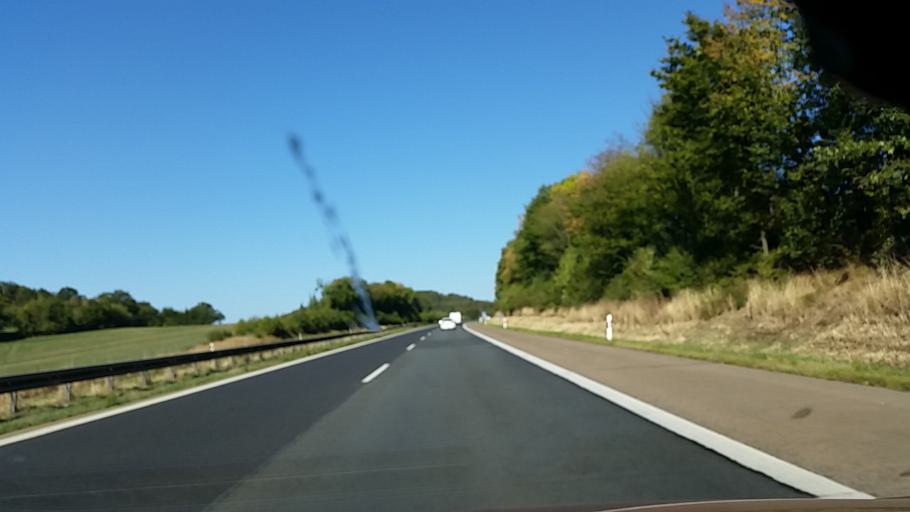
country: DE
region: Bavaria
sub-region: Regierungsbezirk Unterfranken
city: Schondra
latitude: 50.2803
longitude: 9.8661
